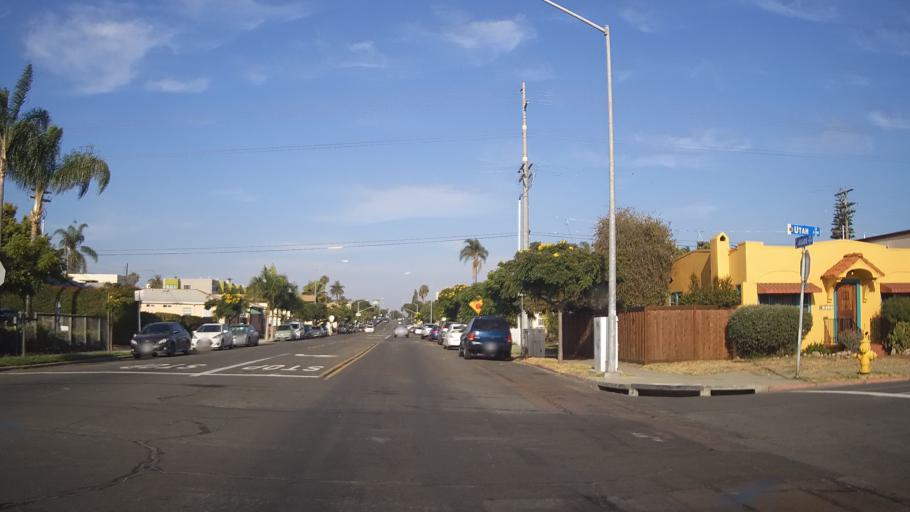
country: US
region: California
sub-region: San Diego County
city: San Diego
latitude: 32.7573
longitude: -117.1327
